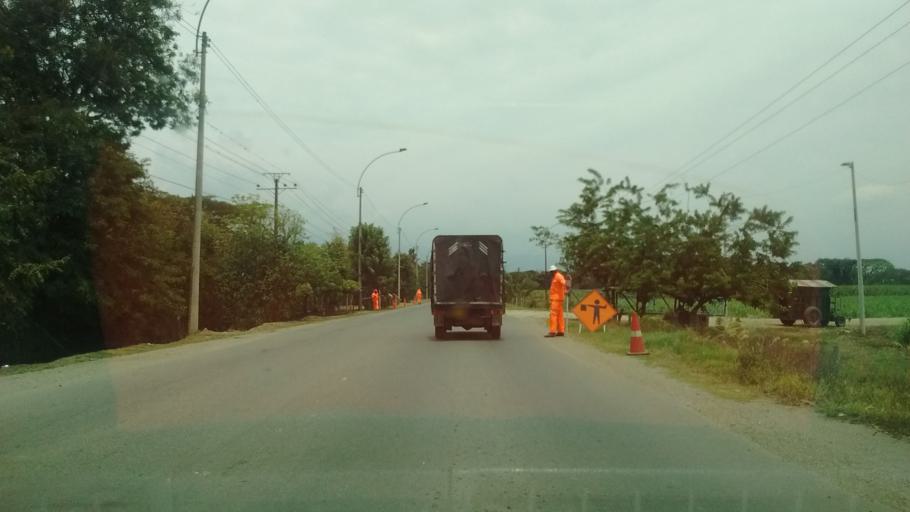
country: CO
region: Valle del Cauca
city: Jamundi
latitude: 3.3178
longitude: -76.4927
